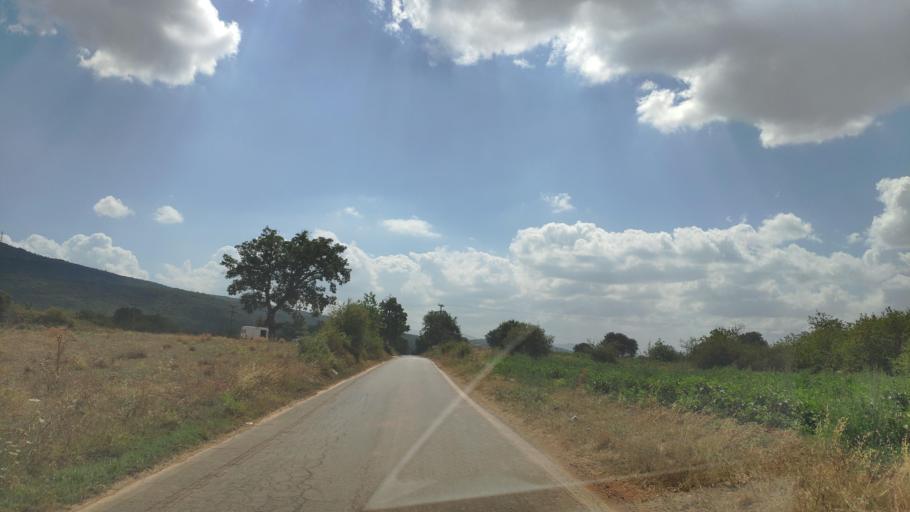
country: GR
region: Peloponnese
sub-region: Nomos Lakonias
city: Kariai
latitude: 37.3181
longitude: 22.4377
